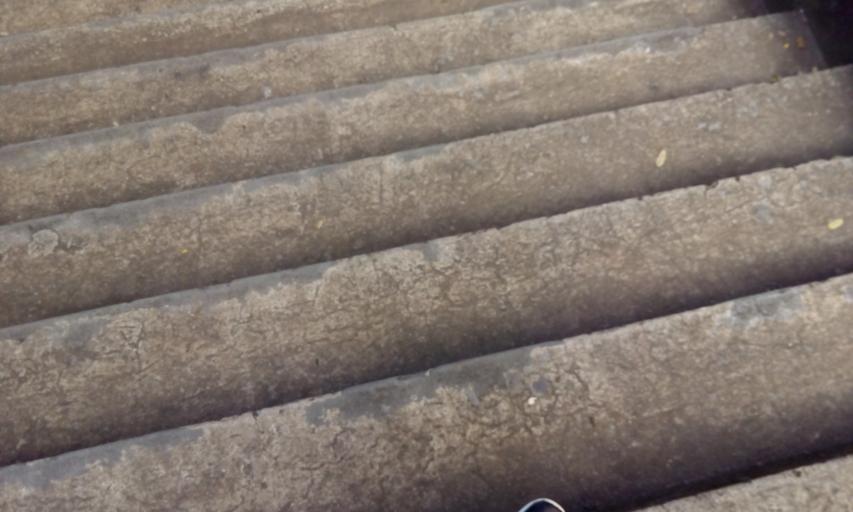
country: BR
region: Bahia
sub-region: Salvador
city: Salvador
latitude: -12.9936
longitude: -38.5209
